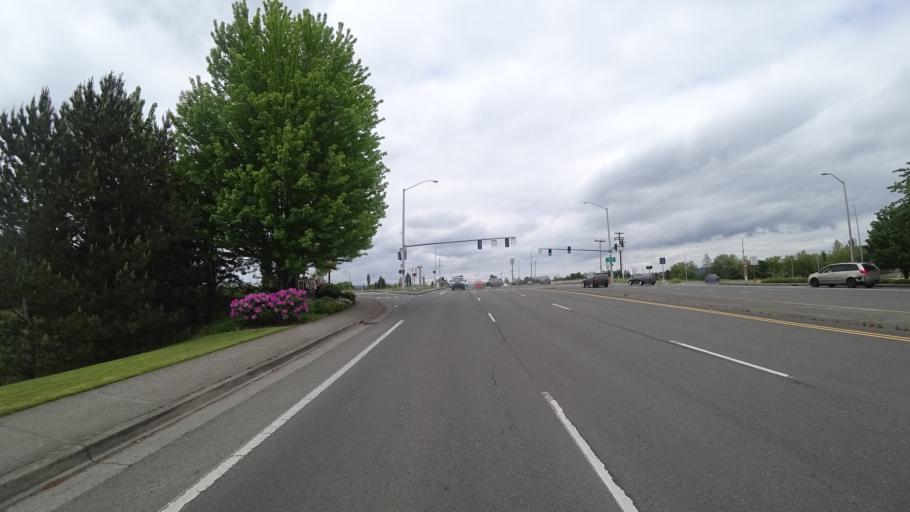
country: US
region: Oregon
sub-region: Washington County
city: Rockcreek
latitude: 45.5405
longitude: -122.8677
